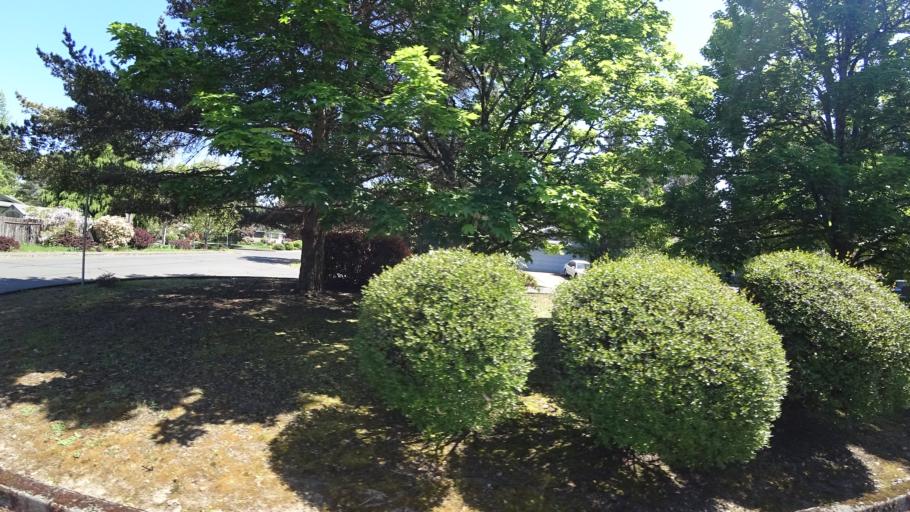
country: US
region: Oregon
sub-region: Washington County
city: Hillsboro
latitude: 45.4988
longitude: -122.9628
